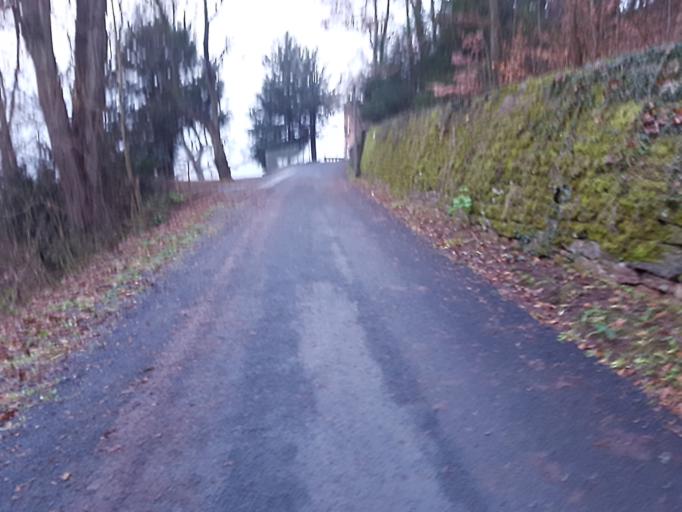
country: DE
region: Bavaria
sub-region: Regierungsbezirk Unterfranken
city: Miltenberg
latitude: 49.6981
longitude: 9.2518
